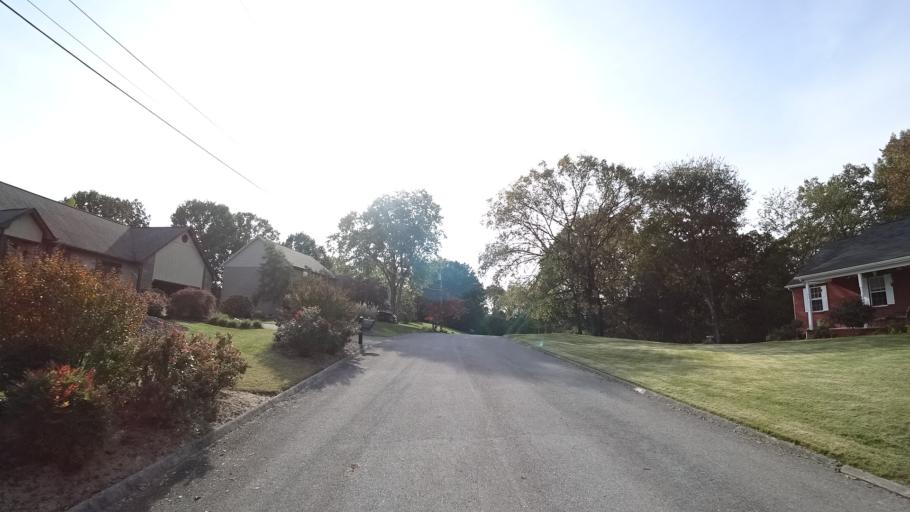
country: US
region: Tennessee
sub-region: Knox County
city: Farragut
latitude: 35.9050
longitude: -84.1624
